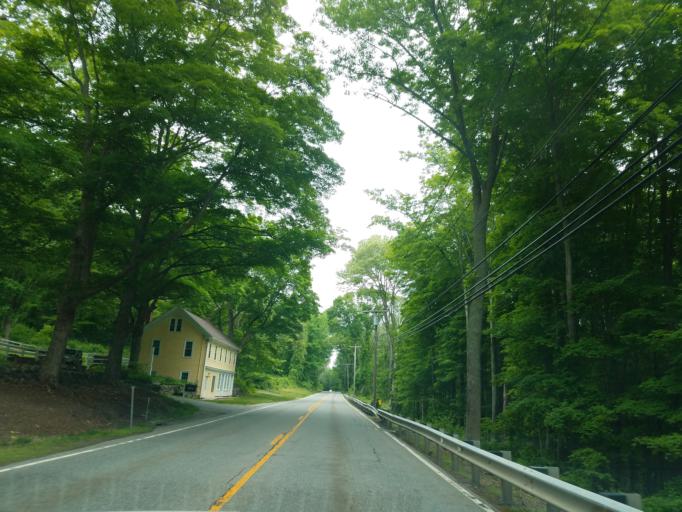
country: US
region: Connecticut
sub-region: New London County
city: Oxoboxo River
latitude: 41.4126
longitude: -72.1870
